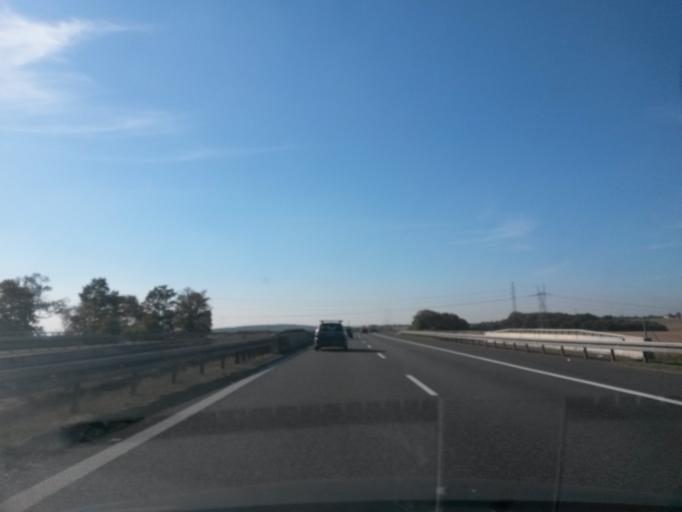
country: PL
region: Opole Voivodeship
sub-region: Powiat krapkowicki
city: Rozwadza
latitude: 50.4775
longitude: 18.0775
